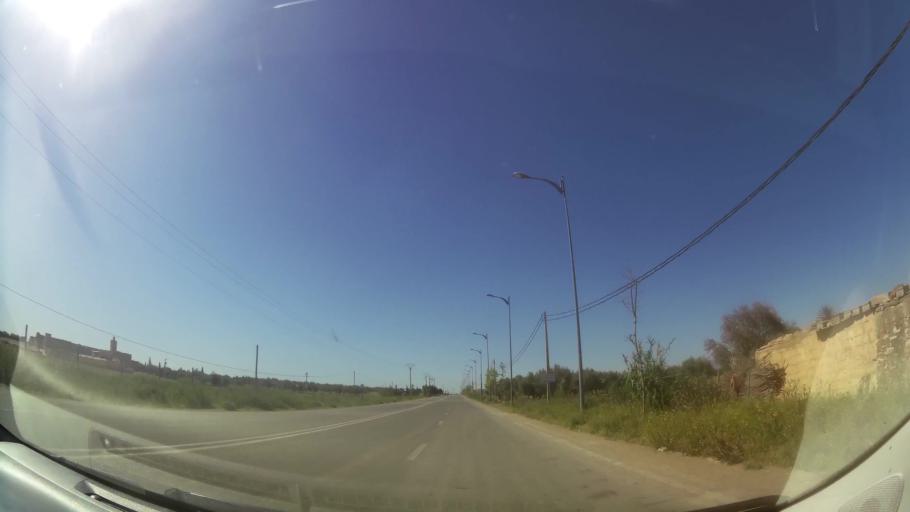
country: MA
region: Oriental
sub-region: Oujda-Angad
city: Oujda
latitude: 34.7205
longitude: -1.8655
